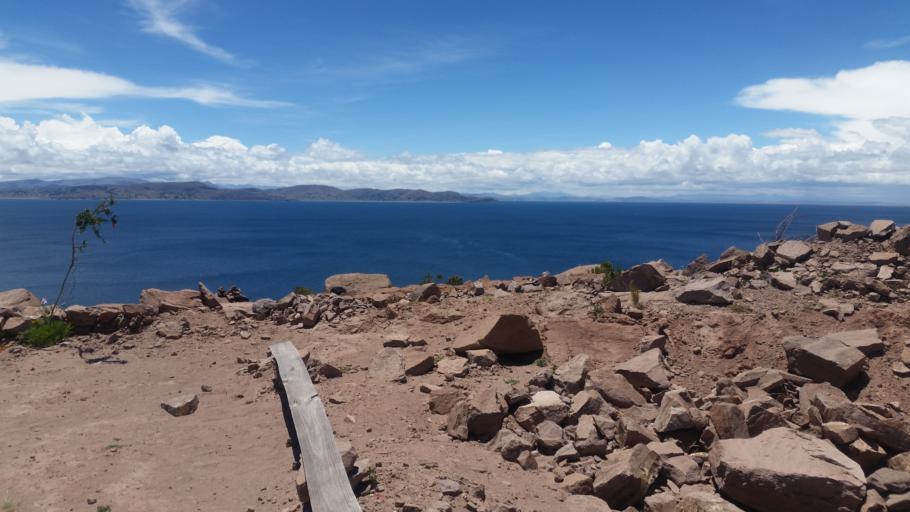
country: PE
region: Puno
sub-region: Provincia de Puno
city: Taquile
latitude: -15.7803
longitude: -69.6833
